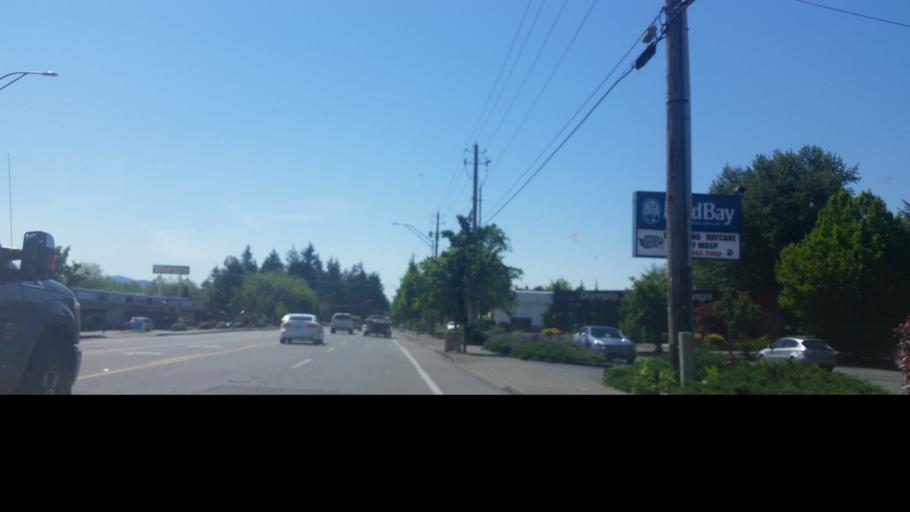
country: US
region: Washington
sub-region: Thurston County
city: Olympia
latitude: 47.0462
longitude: -122.9310
